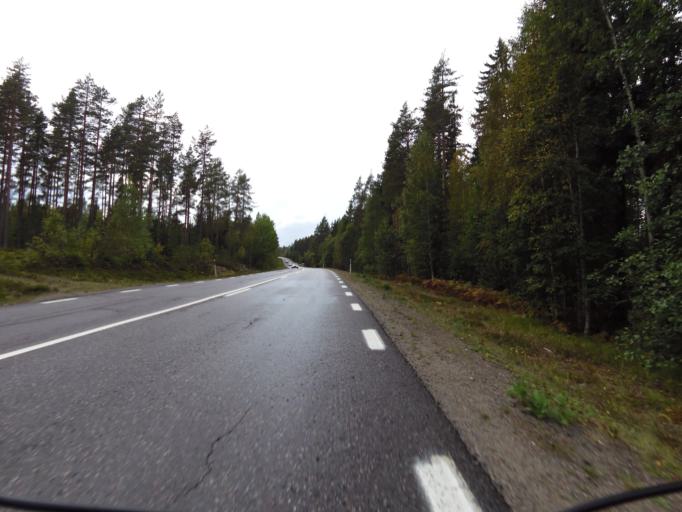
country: SE
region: Gaevleborg
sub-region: Ockelbo Kommun
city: Ockelbo
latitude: 60.8792
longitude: 16.8804
